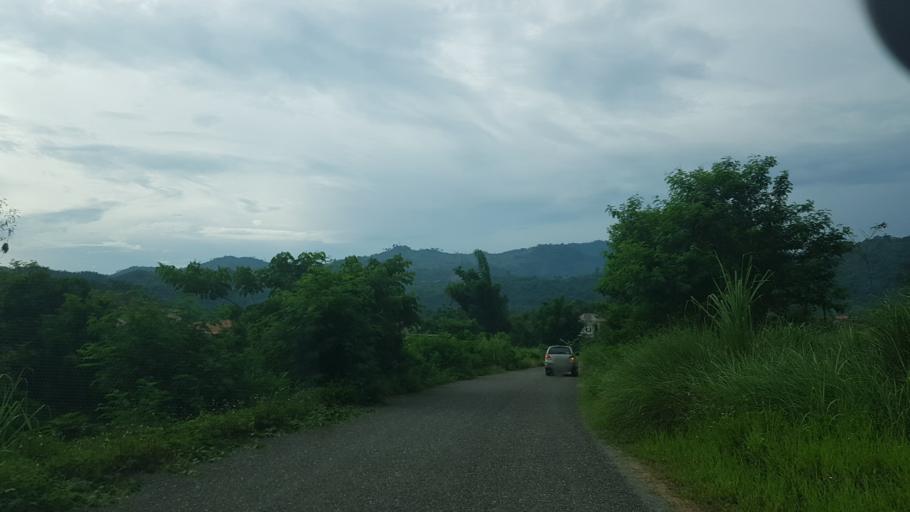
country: LA
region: Oudomxai
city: Muang Xay
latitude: 20.6953
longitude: 101.9899
